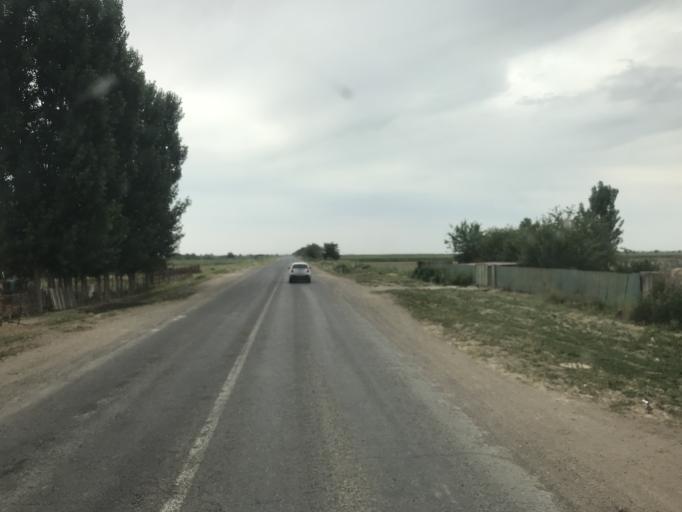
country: KZ
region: Ongtustik Qazaqstan
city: Asykata
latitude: 40.9075
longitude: 68.3523
